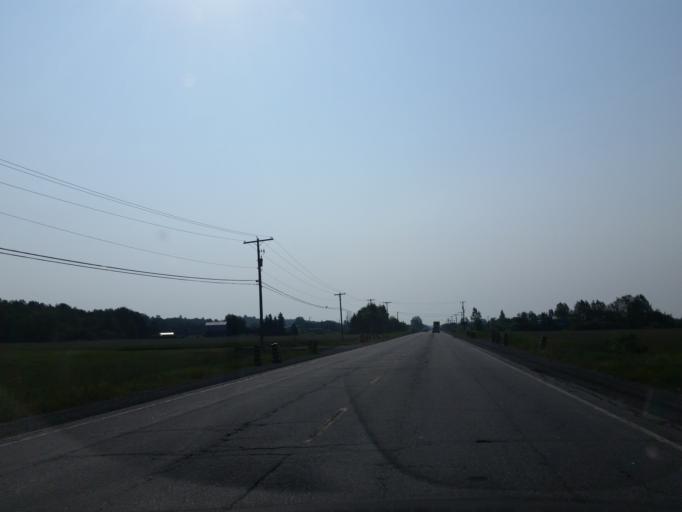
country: CA
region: Ontario
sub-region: Nipissing District
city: North Bay
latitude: 46.4165
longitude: -80.1432
